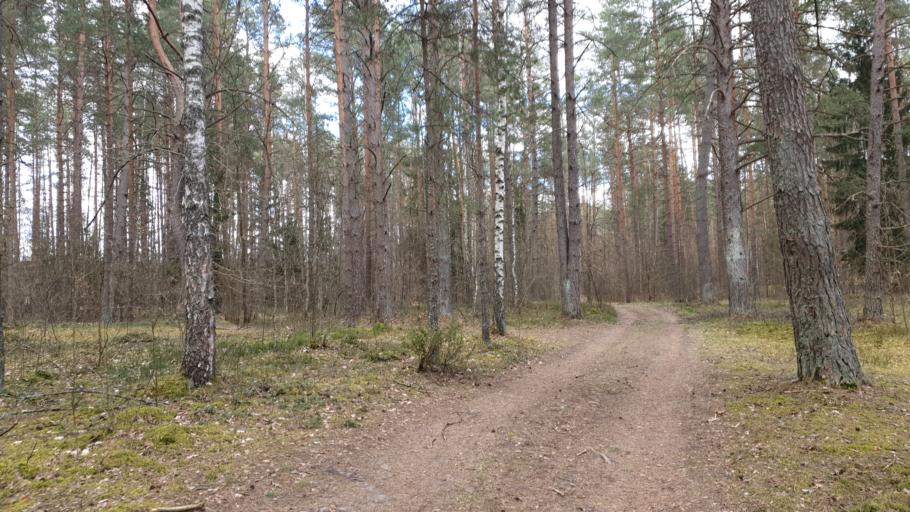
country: LT
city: Grigiskes
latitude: 54.7297
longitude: 25.0307
